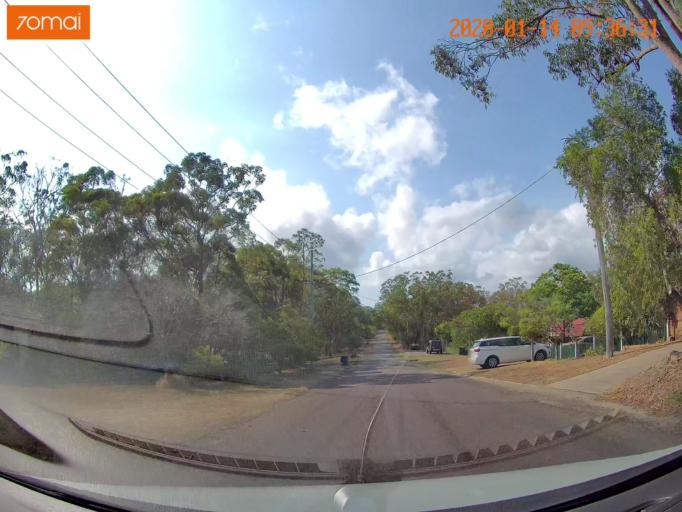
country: AU
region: New South Wales
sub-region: Wyong Shire
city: Kingfisher Shores
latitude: -33.1119
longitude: 151.5568
